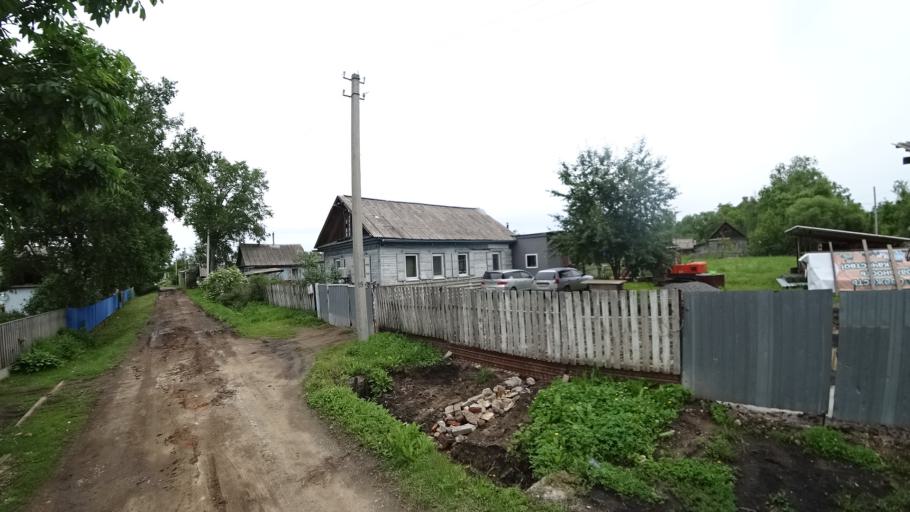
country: RU
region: Primorskiy
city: Novosysoyevka
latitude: 44.2058
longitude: 133.3276
